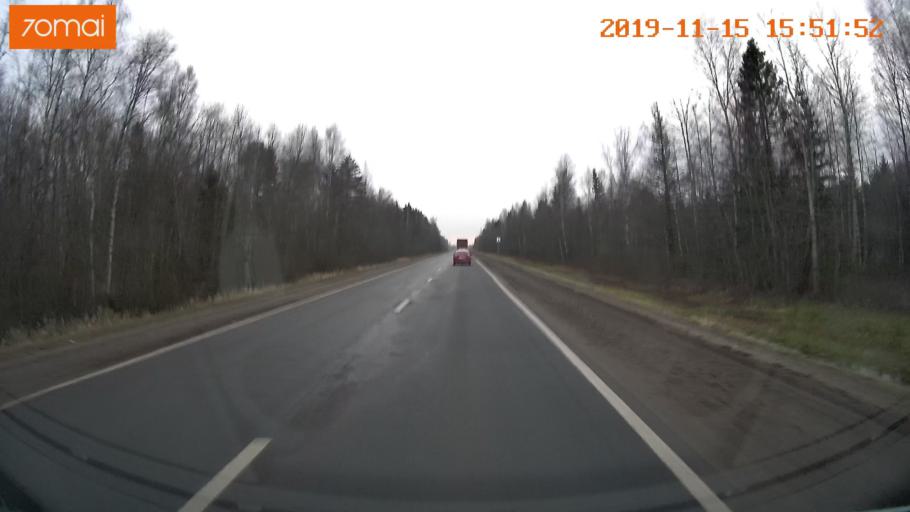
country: RU
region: Jaroslavl
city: Yaroslavl
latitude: 57.8896
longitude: 40.0042
